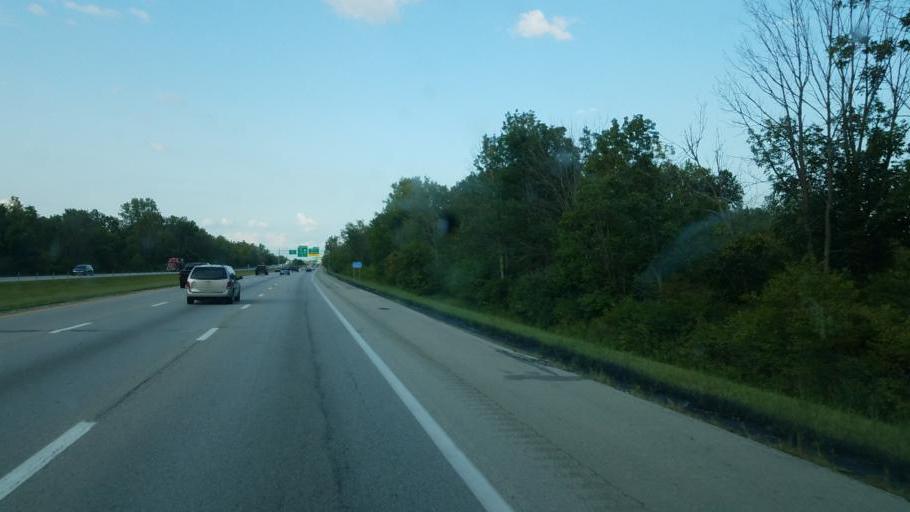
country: US
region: Ohio
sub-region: Franklin County
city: Blacklick Estates
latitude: 39.9226
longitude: -82.8722
